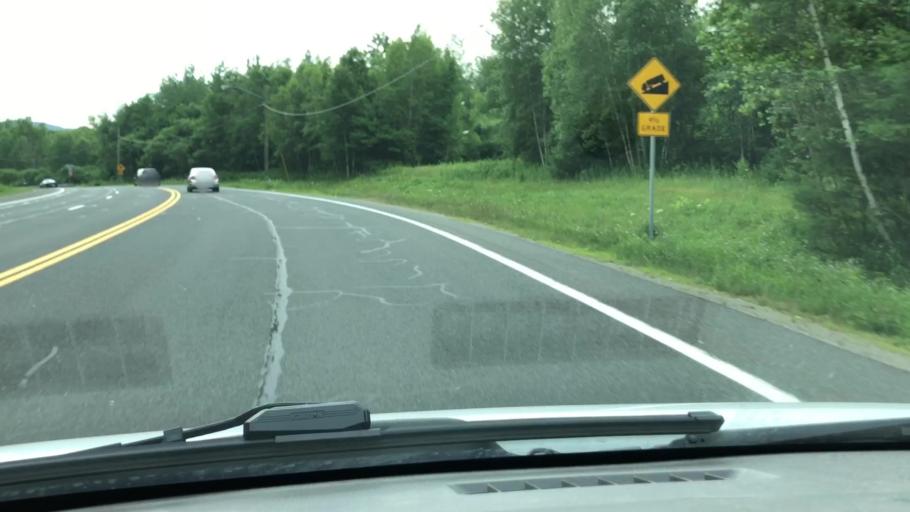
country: US
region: Massachusetts
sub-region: Berkshire County
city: Lanesborough
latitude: 42.4950
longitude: -73.2237
